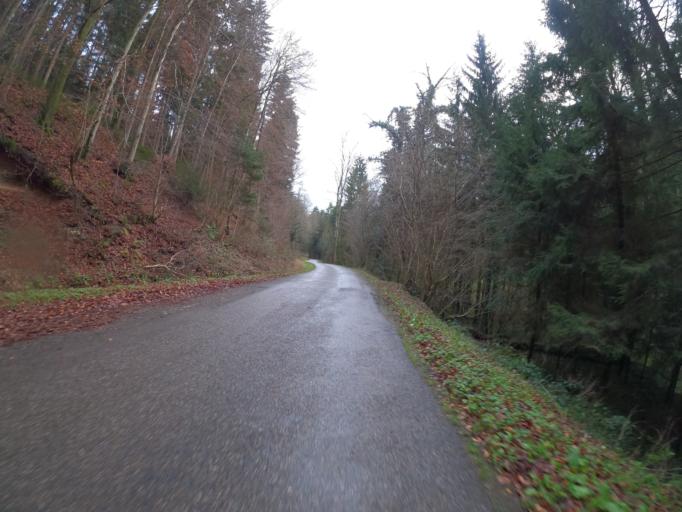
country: DE
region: Baden-Wuerttemberg
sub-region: Regierungsbezirk Stuttgart
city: Lorch
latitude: 48.7850
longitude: 9.7227
